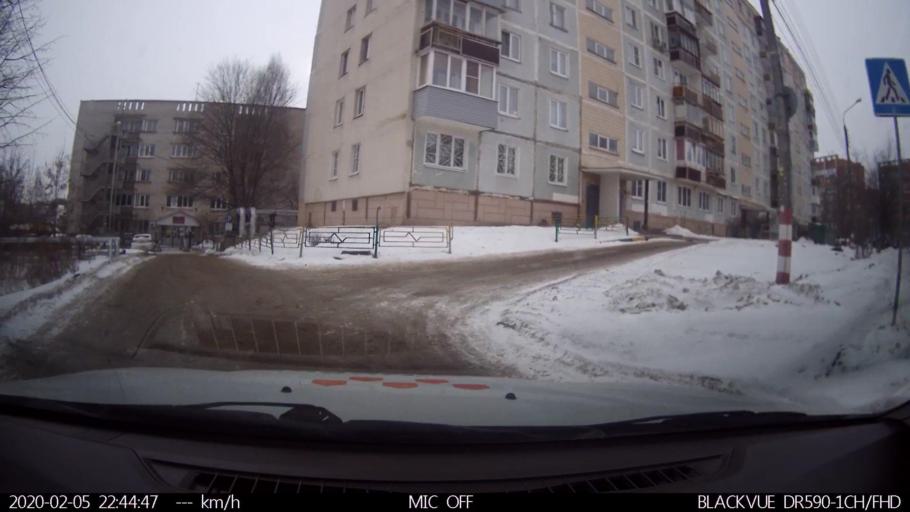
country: RU
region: Nizjnij Novgorod
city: Imeni Stepana Razina
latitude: 54.7048
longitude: 44.4118
